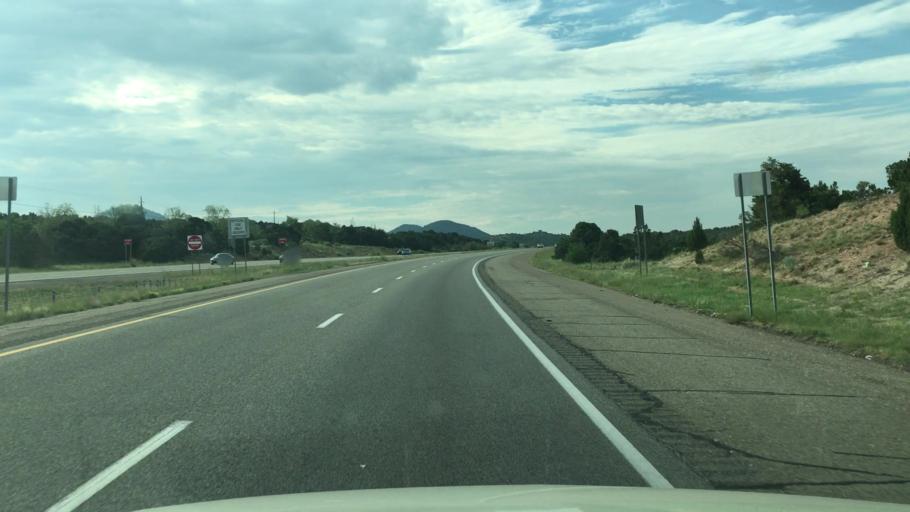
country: US
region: New Mexico
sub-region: Santa Fe County
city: Santa Fe
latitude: 35.6332
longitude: -105.9264
